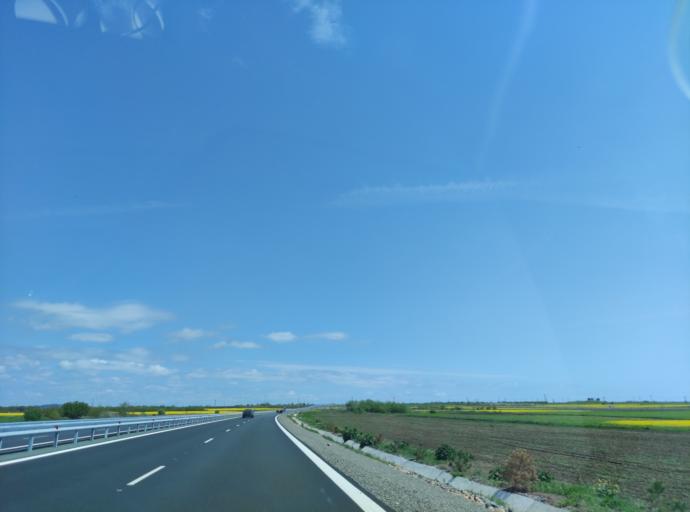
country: BG
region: Burgas
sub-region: Obshtina Pomorie
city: Pomorie
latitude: 42.5723
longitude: 27.5747
